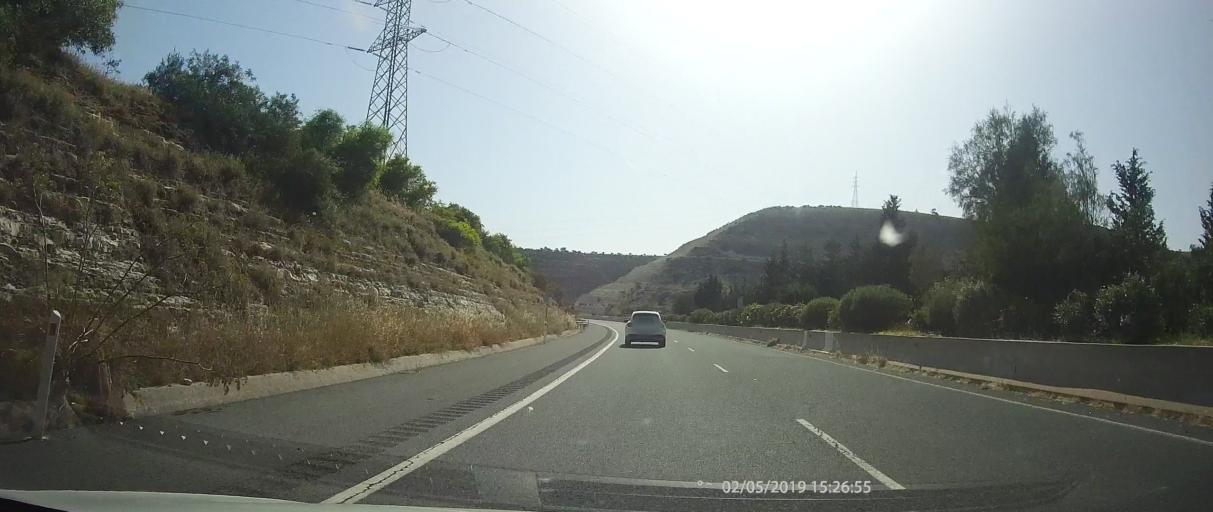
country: CY
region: Limassol
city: Sotira
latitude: 34.7031
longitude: 32.8491
